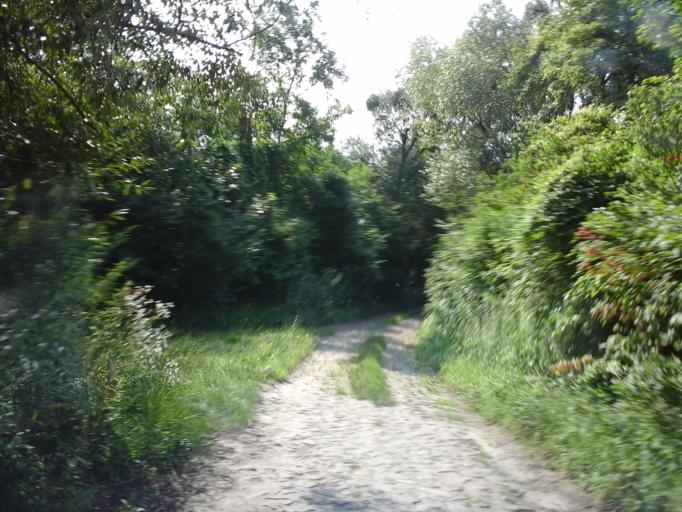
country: PL
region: West Pomeranian Voivodeship
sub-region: Powiat mysliborski
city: Barlinek
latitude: 53.0498
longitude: 15.1972
